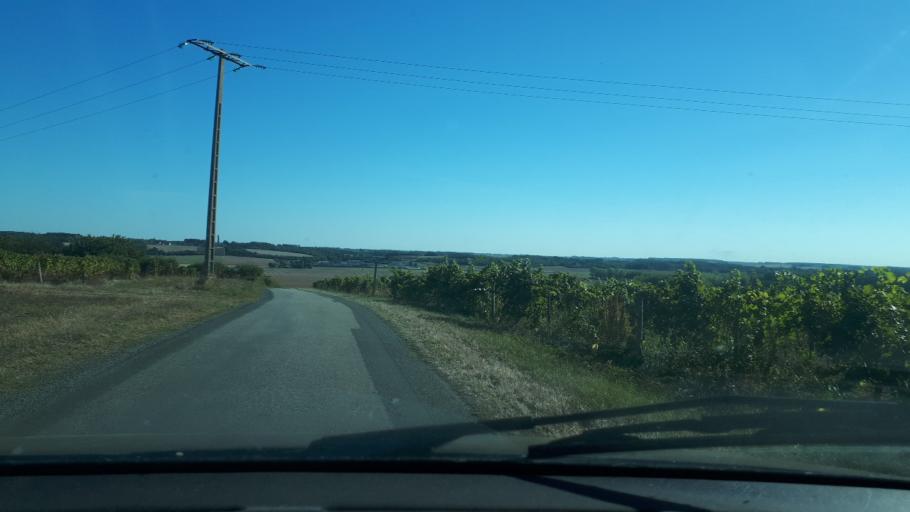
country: FR
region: Centre
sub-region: Departement du Loir-et-Cher
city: Naveil
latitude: 47.7997
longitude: 1.0188
